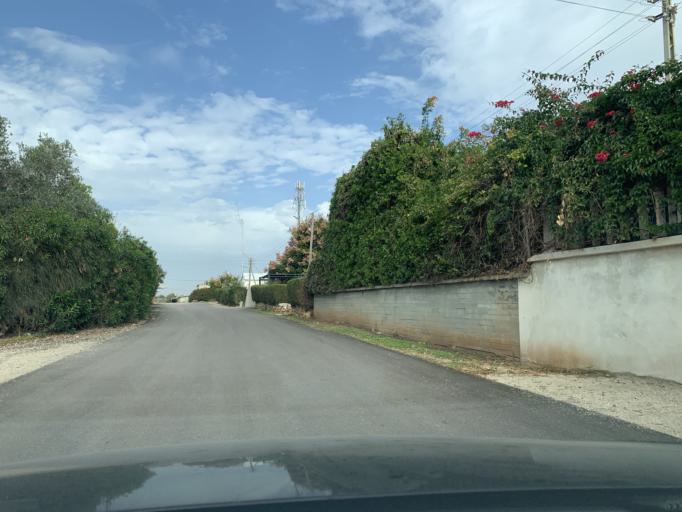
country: IL
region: Central District
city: Et Taiyiba
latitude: 32.2412
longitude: 35.0114
